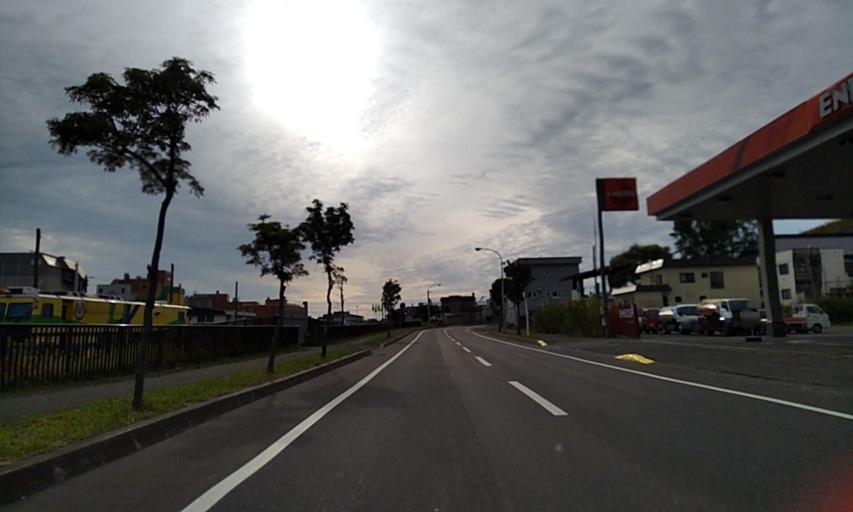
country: JP
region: Hokkaido
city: Wakkanai
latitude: 45.3977
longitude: 141.6824
